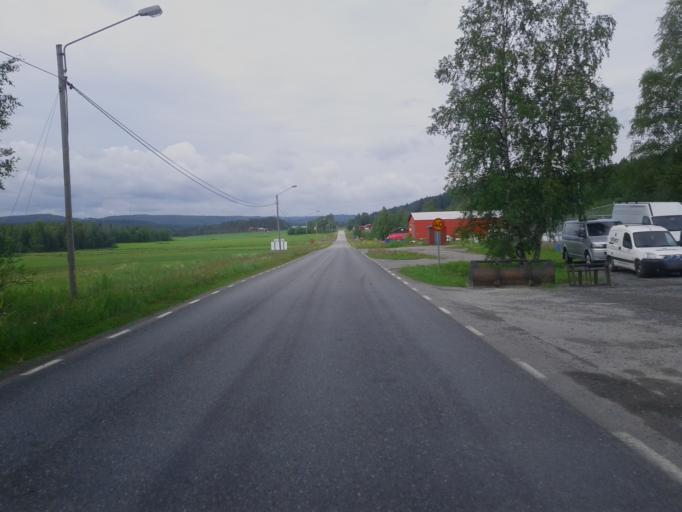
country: SE
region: Vaesterbotten
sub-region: Skelleftea Kommun
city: Forsbacka
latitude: 64.9093
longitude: 20.6101
